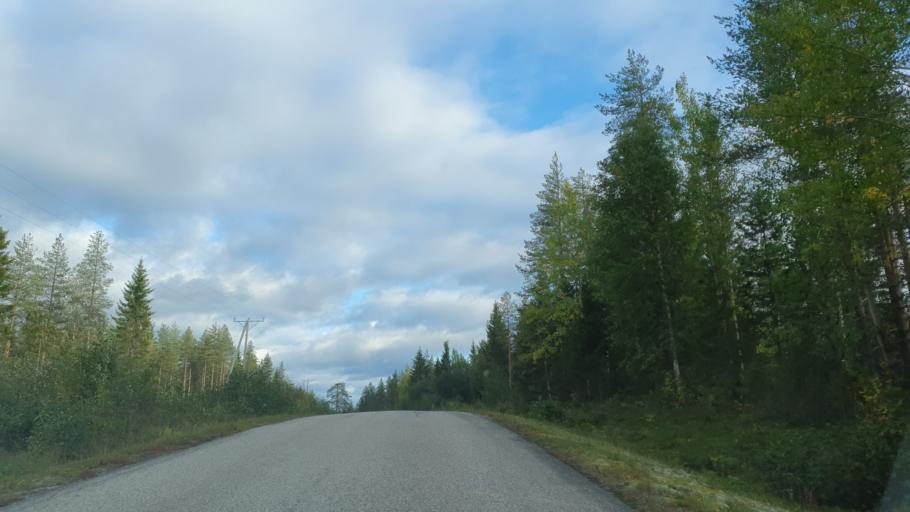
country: FI
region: Kainuu
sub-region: Kehys-Kainuu
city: Kuhmo
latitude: 63.9230
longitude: 30.0428
